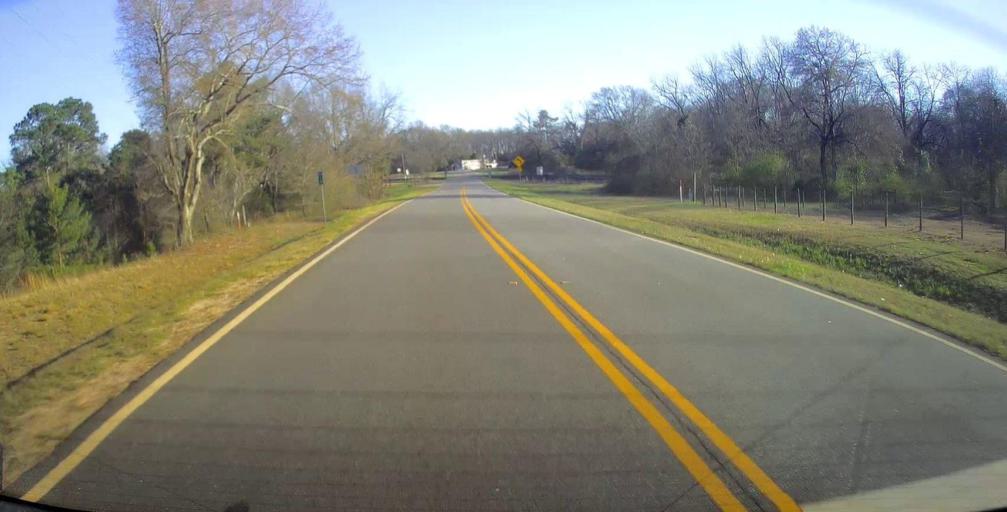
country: US
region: Georgia
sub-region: Taylor County
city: Butler
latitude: 32.5043
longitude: -84.4216
